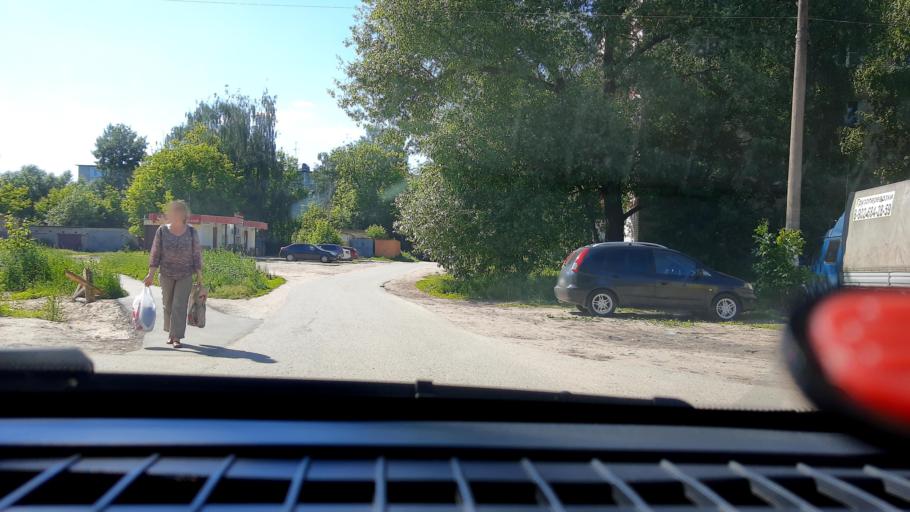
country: RU
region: Nizjnij Novgorod
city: Novaya Balakhna
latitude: 56.5200
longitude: 43.5627
